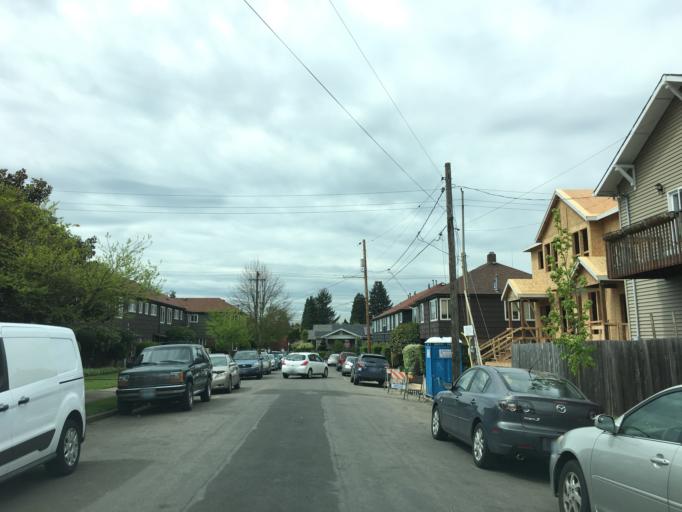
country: US
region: Oregon
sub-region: Multnomah County
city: Lents
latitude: 45.5259
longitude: -122.6010
